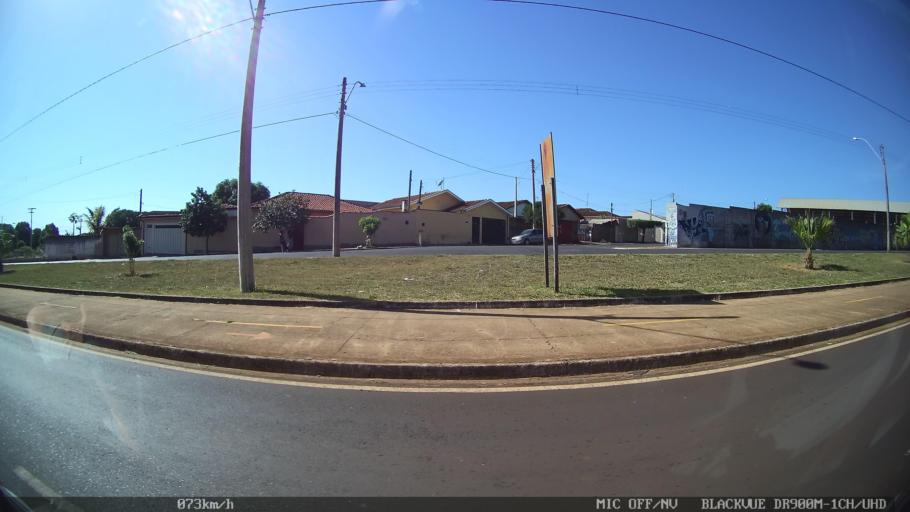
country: BR
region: Sao Paulo
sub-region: Batatais
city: Batatais
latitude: -20.9110
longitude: -47.5828
